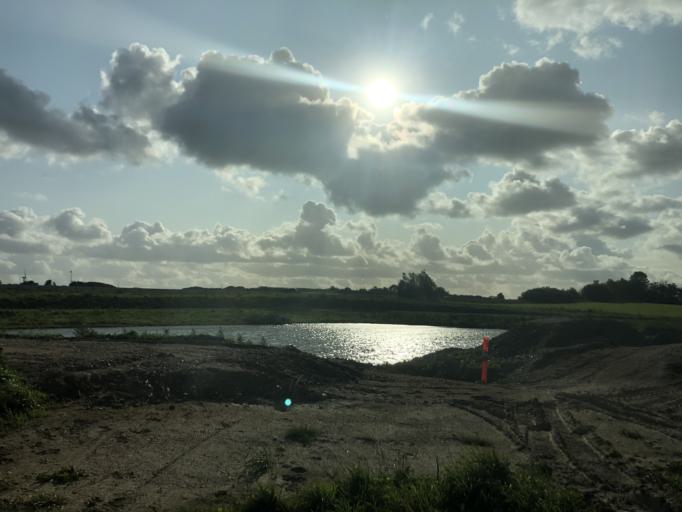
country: DK
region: Zealand
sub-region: Holbaek Kommune
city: Holbaek
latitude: 55.6581
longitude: 11.6469
